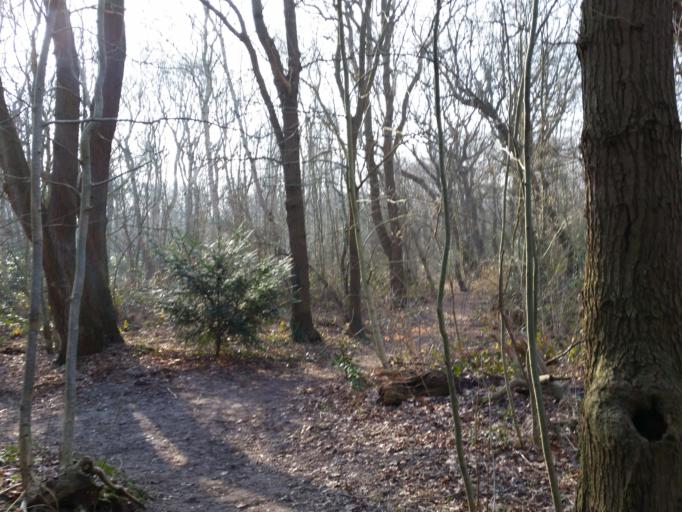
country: NL
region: South Holland
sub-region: Gemeente Westland
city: Poeldijk
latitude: 52.0500
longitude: 4.2154
